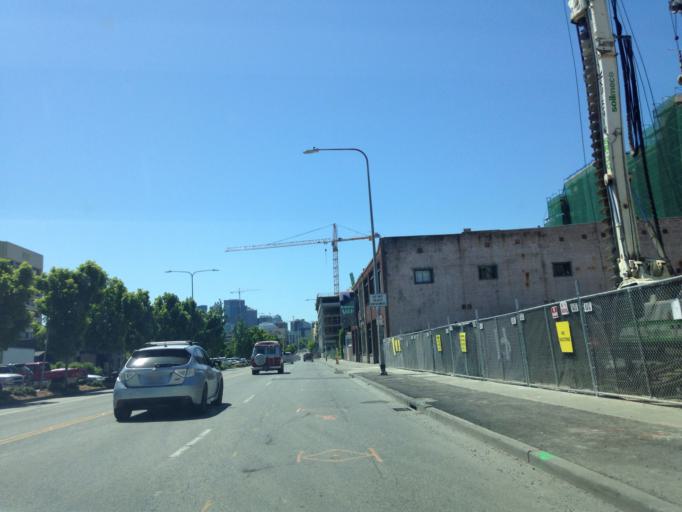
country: US
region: Washington
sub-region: King County
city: Seattle
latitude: 47.6319
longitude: -122.3411
